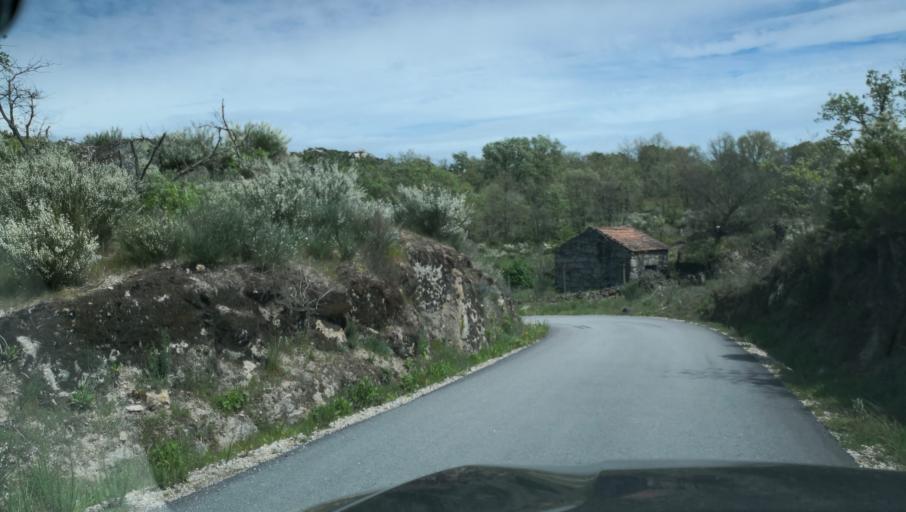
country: PT
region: Vila Real
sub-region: Vila Real
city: Vila Real
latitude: 41.3637
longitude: -7.6706
